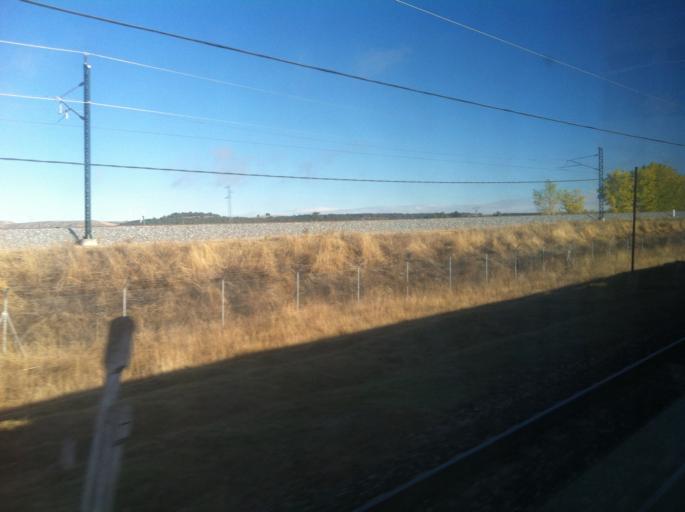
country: ES
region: Castille and Leon
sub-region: Provincia de Palencia
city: Villodrigo
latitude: 42.1543
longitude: -4.0937
